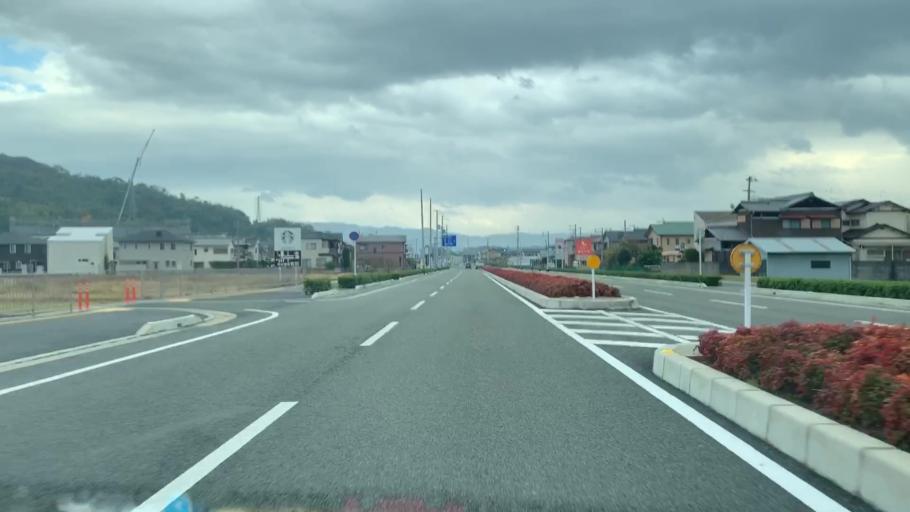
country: JP
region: Wakayama
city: Wakayama-shi
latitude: 34.2189
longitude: 135.2074
